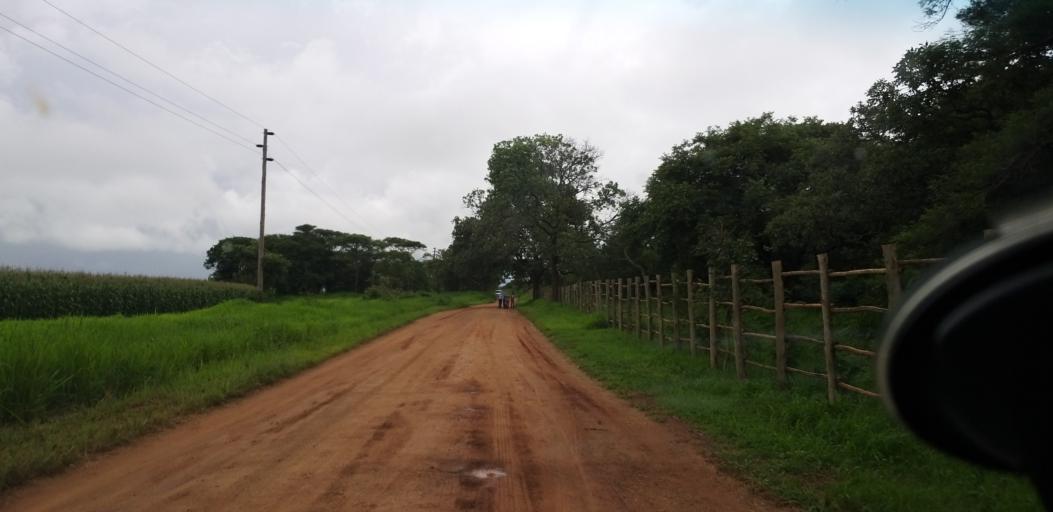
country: ZM
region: Lusaka
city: Lusaka
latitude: -15.5295
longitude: 28.3101
